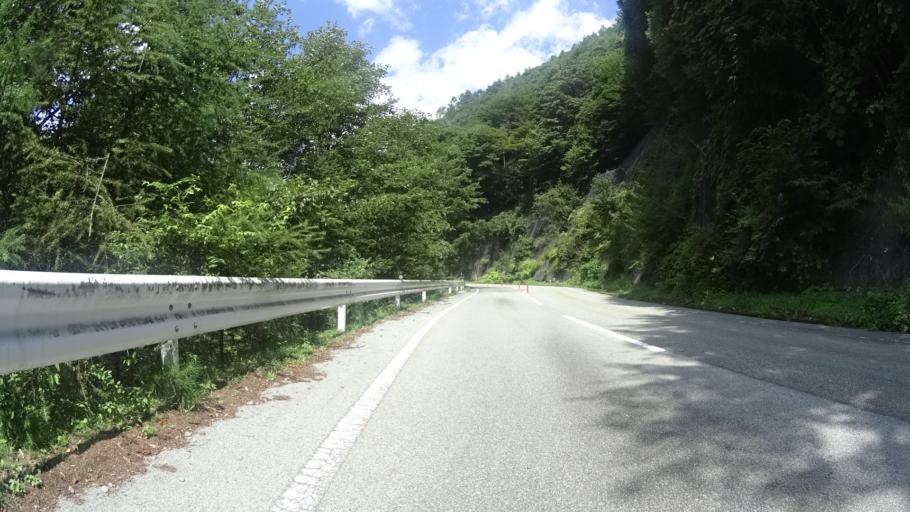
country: JP
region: Yamanashi
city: Enzan
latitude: 35.8010
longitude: 138.6727
